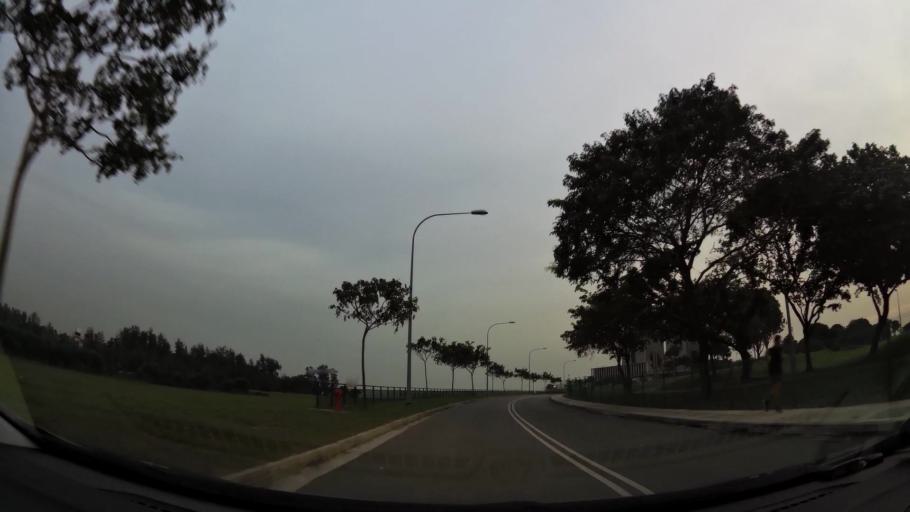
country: SG
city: Singapore
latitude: 1.2864
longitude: 103.8777
